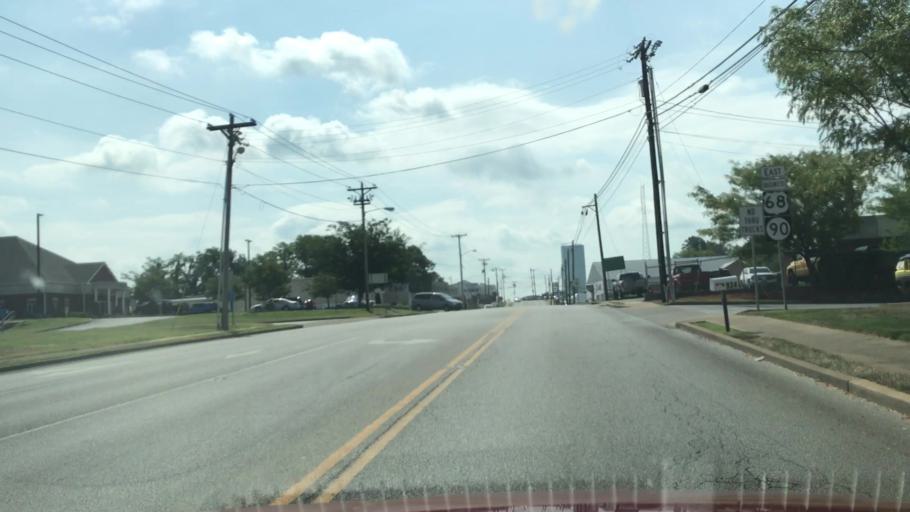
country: US
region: Kentucky
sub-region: Barren County
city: Glasgow
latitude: 37.0017
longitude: -85.9260
